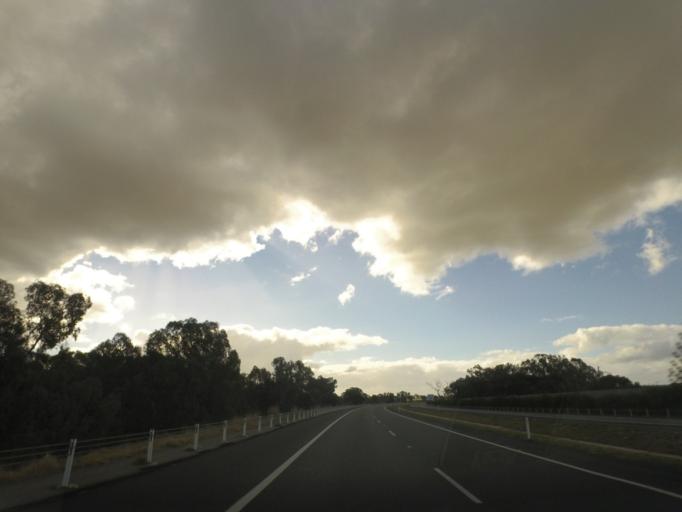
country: AU
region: New South Wales
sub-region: Greater Hume Shire
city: Holbrook
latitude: -35.7206
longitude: 147.3027
